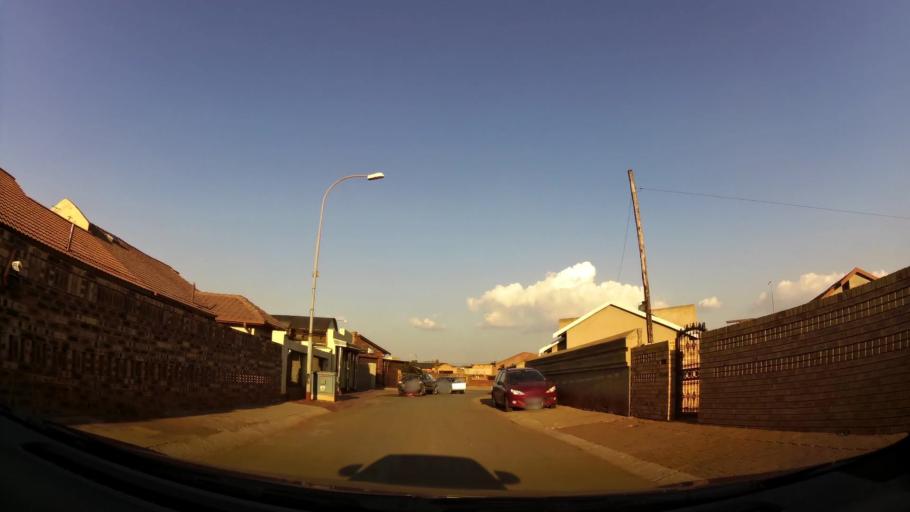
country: ZA
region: Gauteng
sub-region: City of Johannesburg Metropolitan Municipality
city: Soweto
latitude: -26.2236
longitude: 27.8557
